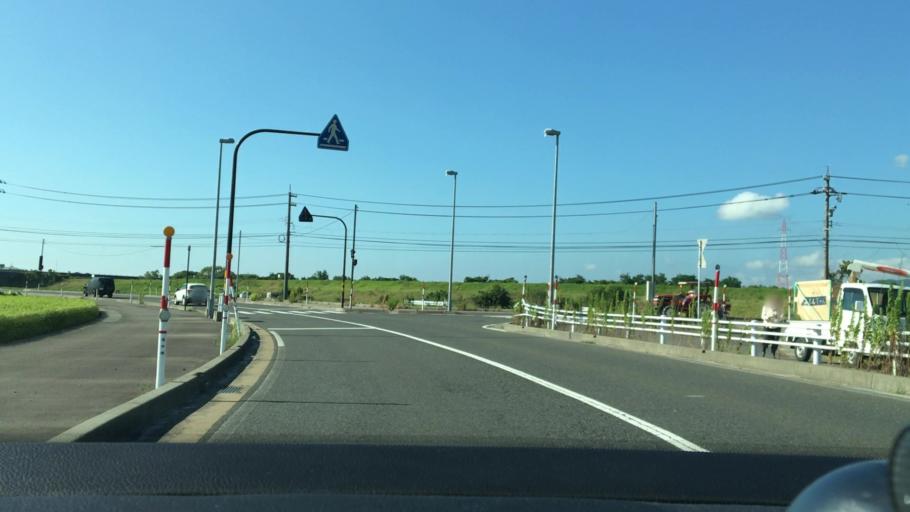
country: JP
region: Fukui
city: Maruoka
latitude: 36.0956
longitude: 136.2816
